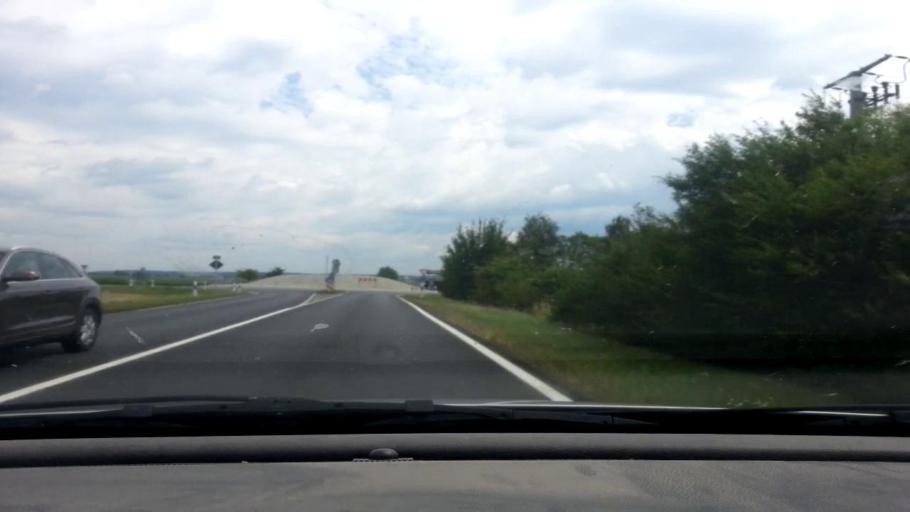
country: DE
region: Bavaria
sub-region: Upper Palatinate
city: Mitterteich
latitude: 49.9367
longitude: 12.2319
